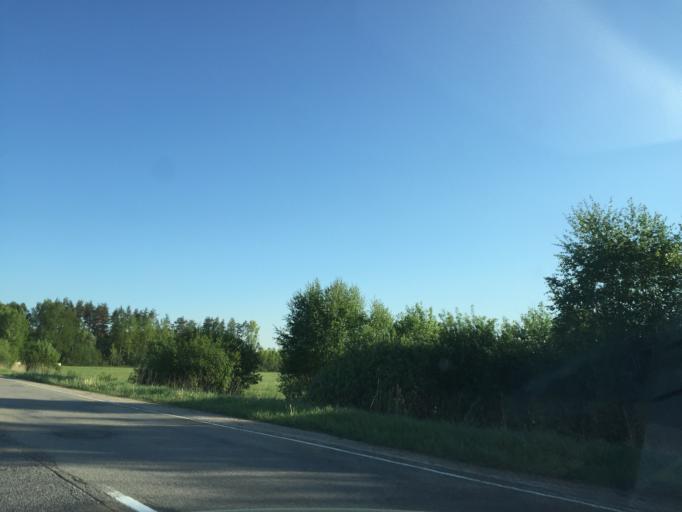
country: LV
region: Kekava
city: Kekava
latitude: 56.7733
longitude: 24.3036
